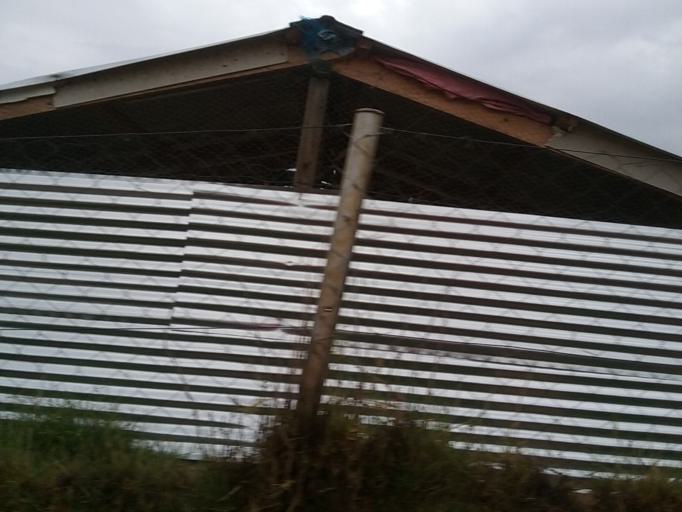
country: LS
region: Berea
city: Teyateyaneng
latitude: -29.1263
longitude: 27.7455
